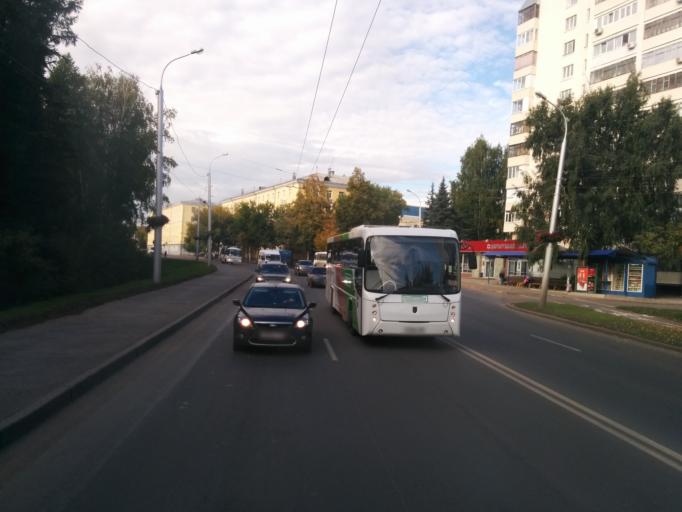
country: RU
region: Bashkortostan
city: Ufa
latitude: 54.8159
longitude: 56.0576
